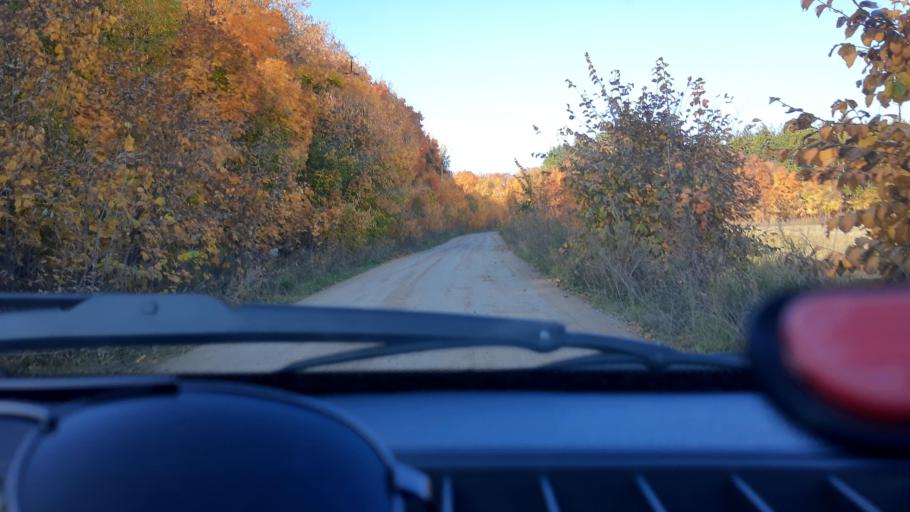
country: RU
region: Bashkortostan
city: Karmaskaly
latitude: 54.3760
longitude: 55.9104
